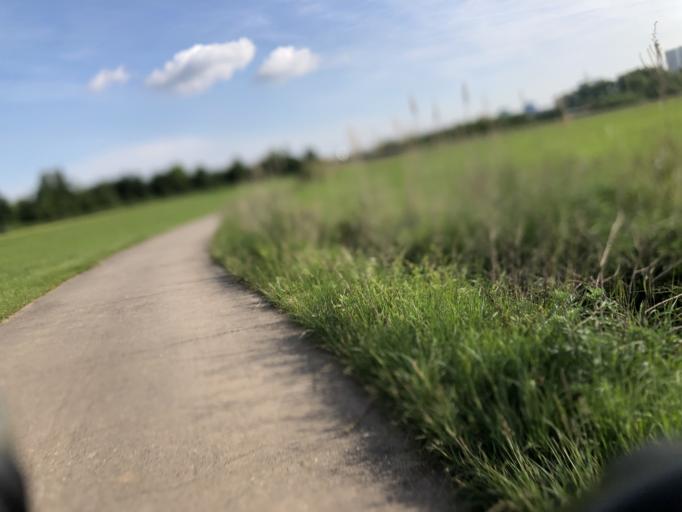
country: DE
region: Bavaria
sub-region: Regierungsbezirk Mittelfranken
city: Erlangen
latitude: 49.5731
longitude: 10.9760
